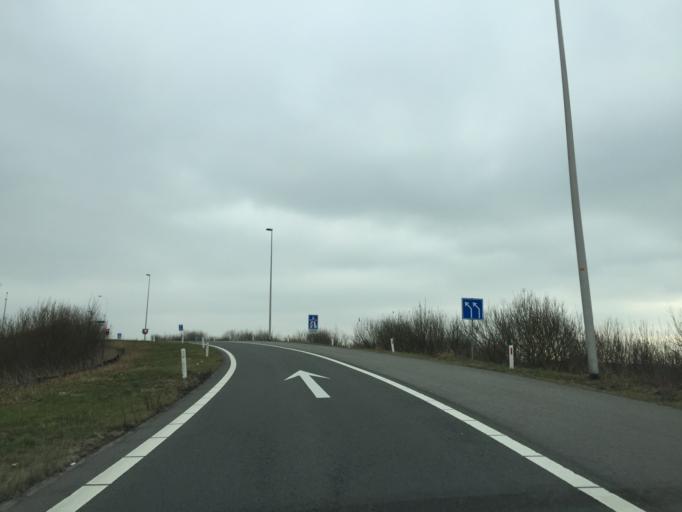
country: NL
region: Utrecht
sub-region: Gemeente Montfoort
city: Montfoort
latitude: 52.0794
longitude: 4.9759
